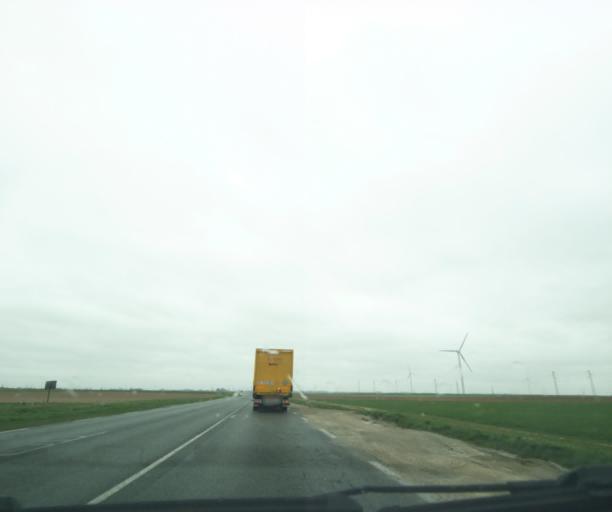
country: FR
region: Centre
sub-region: Departement d'Eure-et-Loir
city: Toury
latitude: 48.1807
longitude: 1.9270
